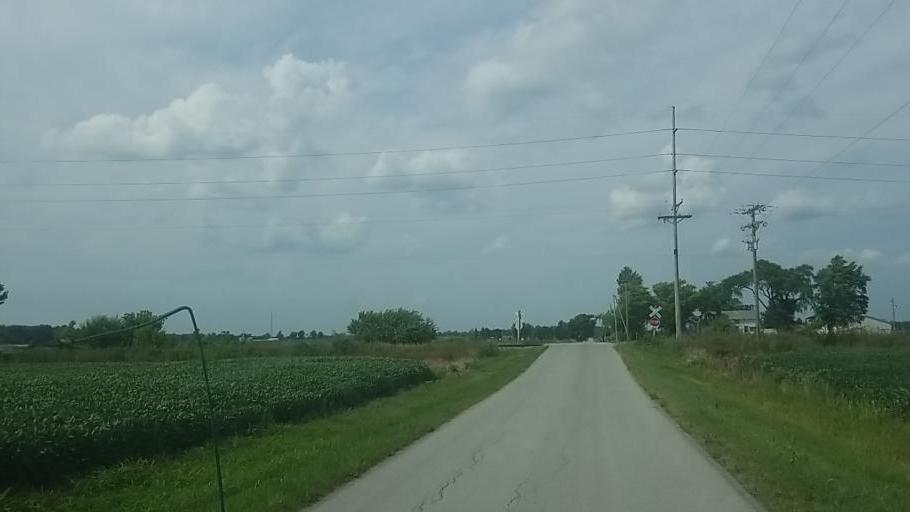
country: US
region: Ohio
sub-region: Hardin County
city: Forest
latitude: 40.8063
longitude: -83.4675
